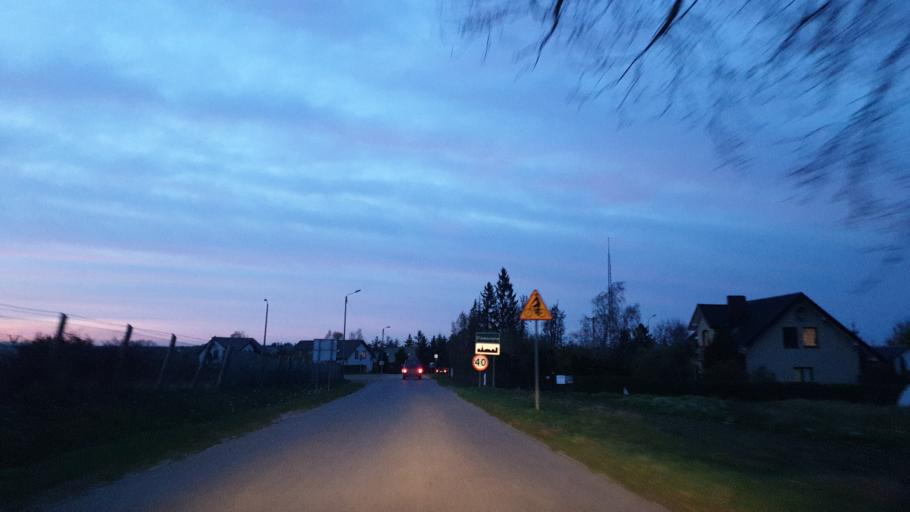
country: PL
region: Pomeranian Voivodeship
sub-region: Powiat pucki
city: Krokowa
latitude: 54.7830
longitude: 18.2000
